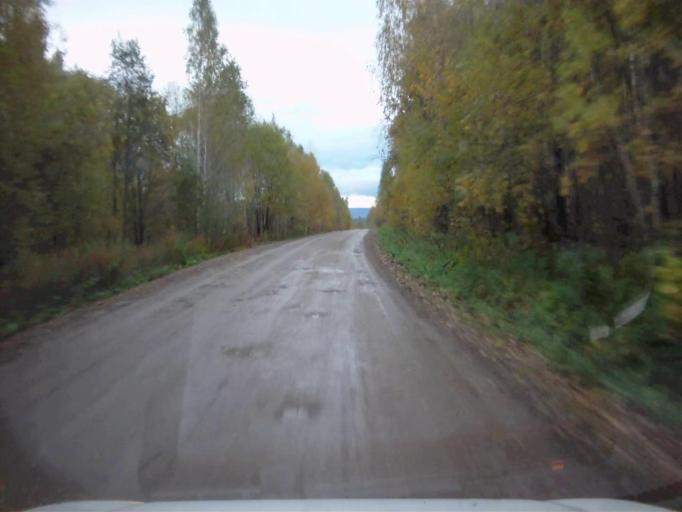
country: RU
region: Sverdlovsk
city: Mikhaylovsk
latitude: 56.1930
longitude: 59.1943
